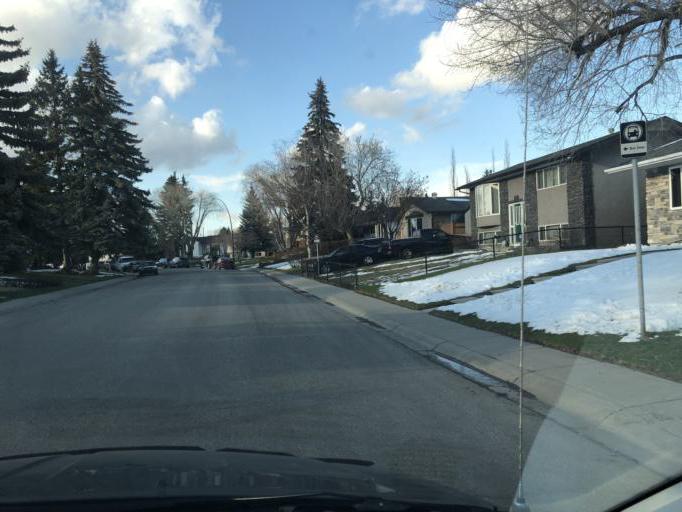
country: CA
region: Alberta
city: Calgary
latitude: 50.9443
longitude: -114.0294
